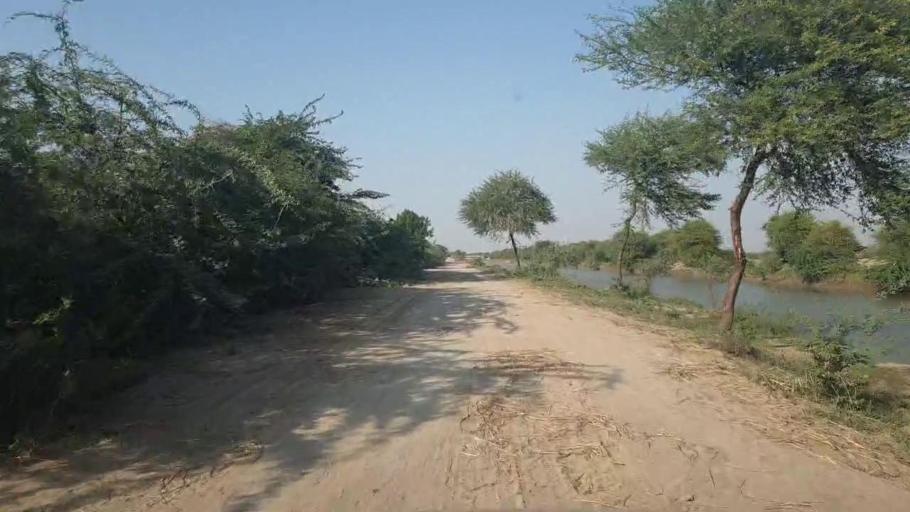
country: PK
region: Sindh
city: Badin
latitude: 24.6336
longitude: 68.8150
